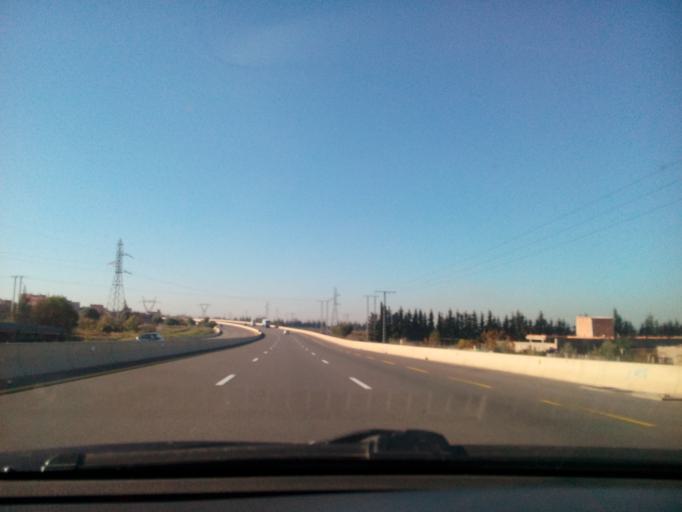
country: DZ
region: Chlef
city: Oued Sly
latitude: 36.0861
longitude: 1.1910
